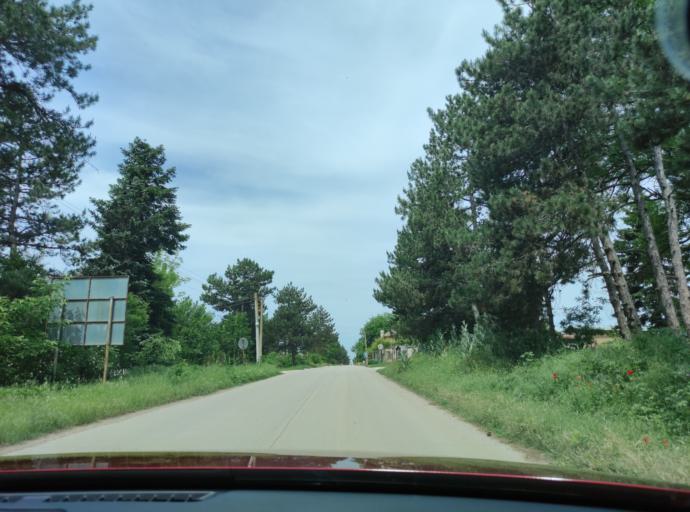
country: BG
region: Pleven
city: Iskur
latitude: 43.5356
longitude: 24.2887
